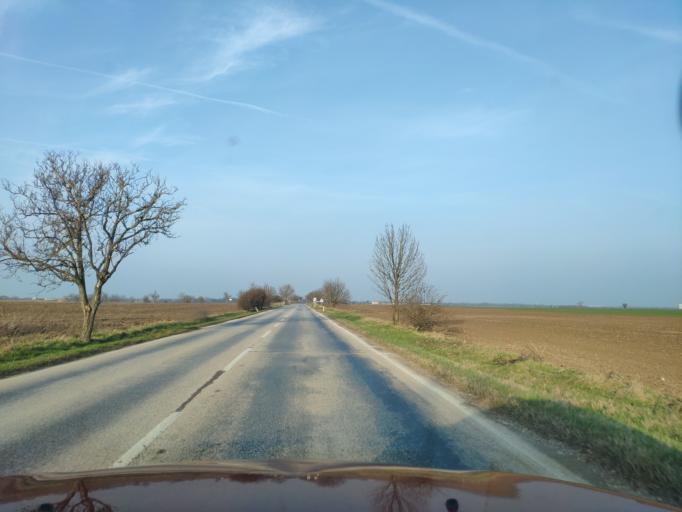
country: SK
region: Bratislavsky
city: Senec
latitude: 48.2974
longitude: 17.4665
